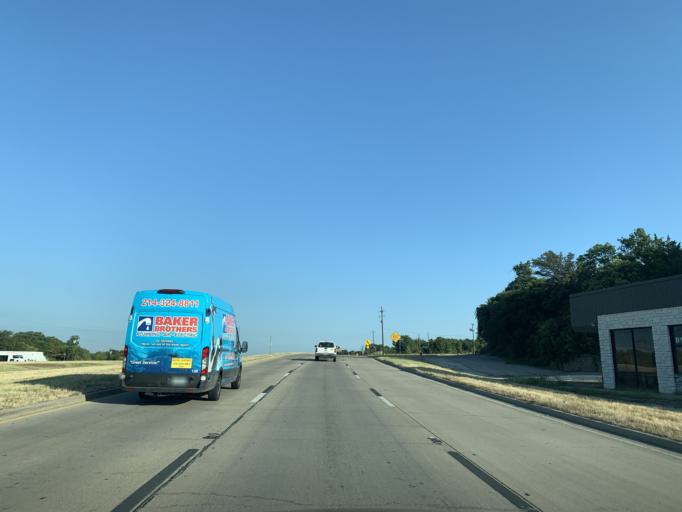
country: US
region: Texas
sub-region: Tarrant County
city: Lake Worth
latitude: 32.8173
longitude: -97.4408
